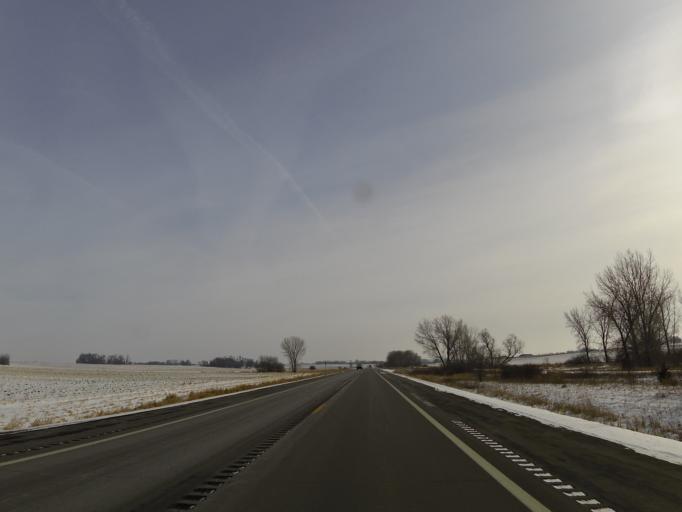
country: US
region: Minnesota
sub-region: McLeod County
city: Hutchinson
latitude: 44.9152
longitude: -94.4576
